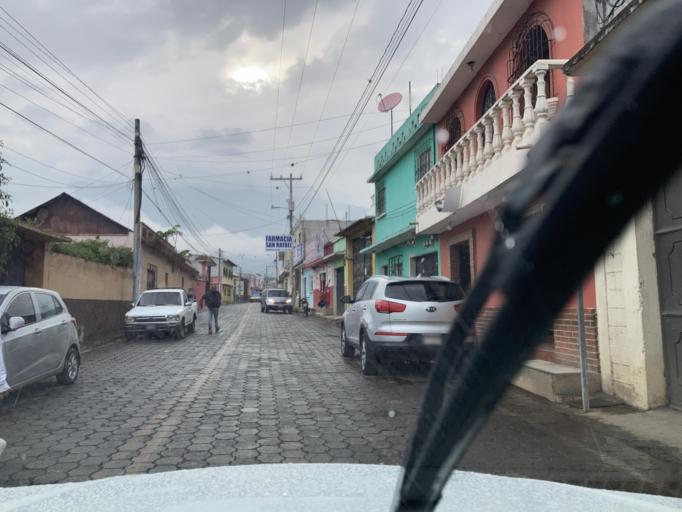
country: GT
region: Sacatepequez
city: San Miguel Duenas
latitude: 14.5247
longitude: -90.7979
